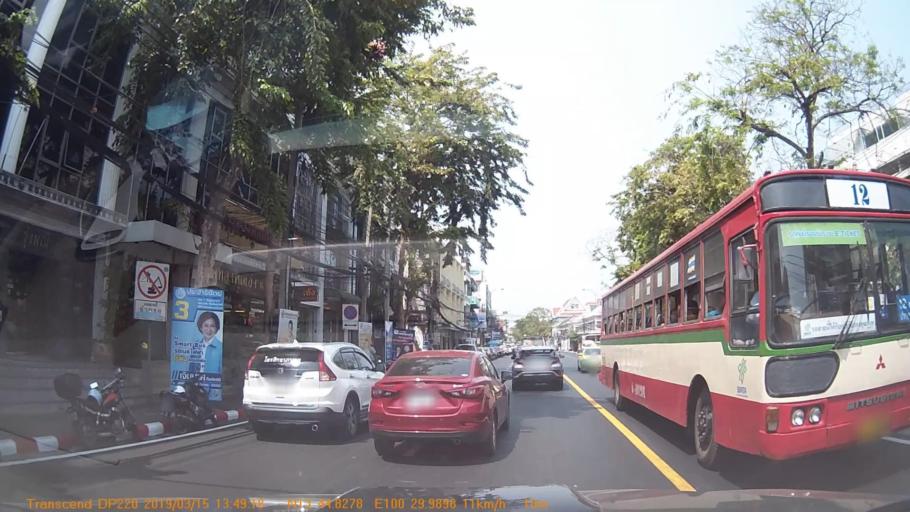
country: TH
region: Bangkok
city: Bangkok
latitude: 13.7472
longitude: 100.4998
